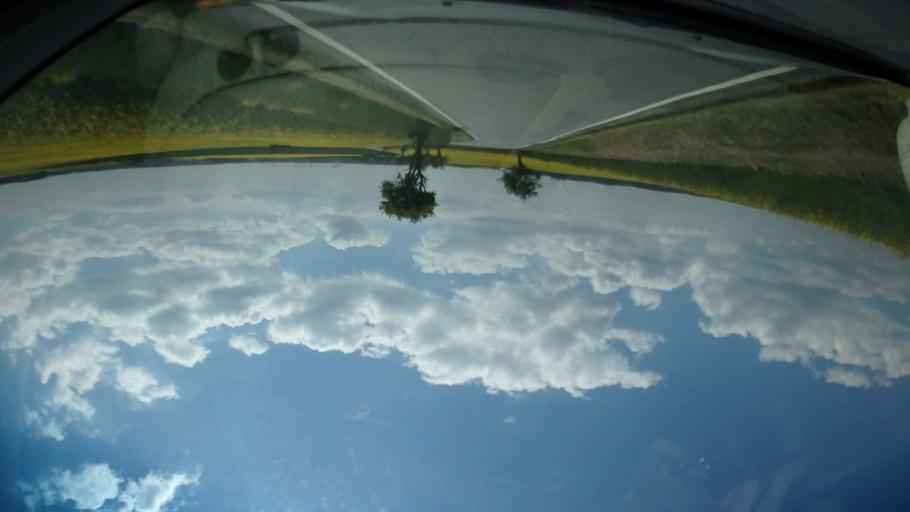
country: CZ
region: Vysocina
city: Hrotovice
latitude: 49.1446
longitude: 16.0765
